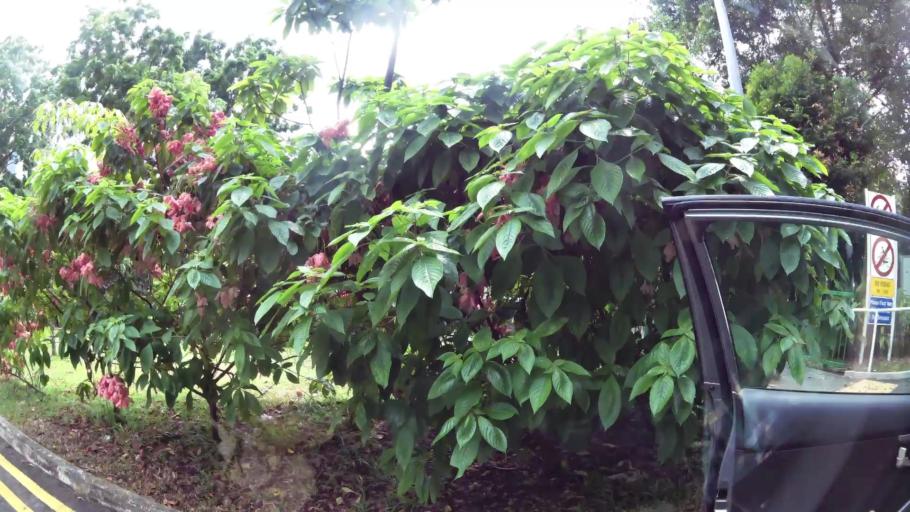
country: SG
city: Singapore
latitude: 1.2816
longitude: 103.8311
